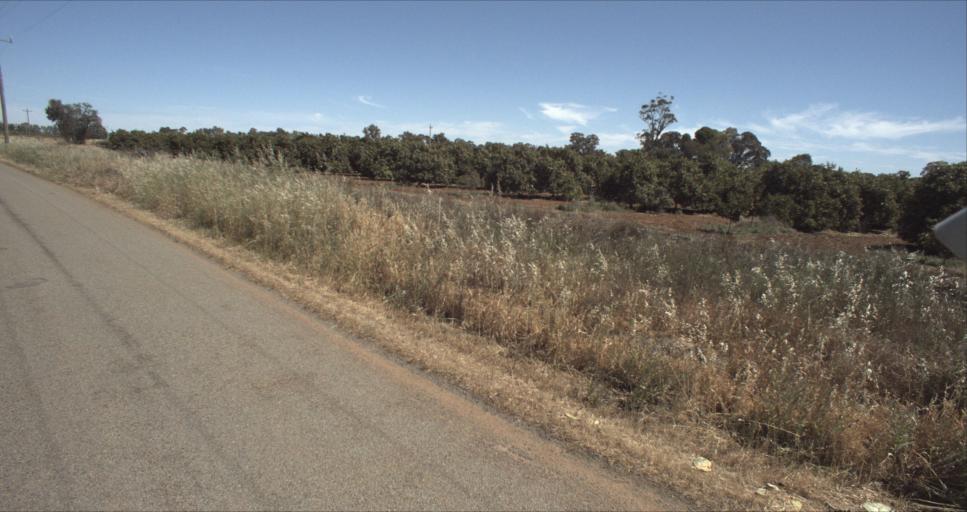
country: AU
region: New South Wales
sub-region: Leeton
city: Leeton
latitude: -34.5278
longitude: 146.3459
